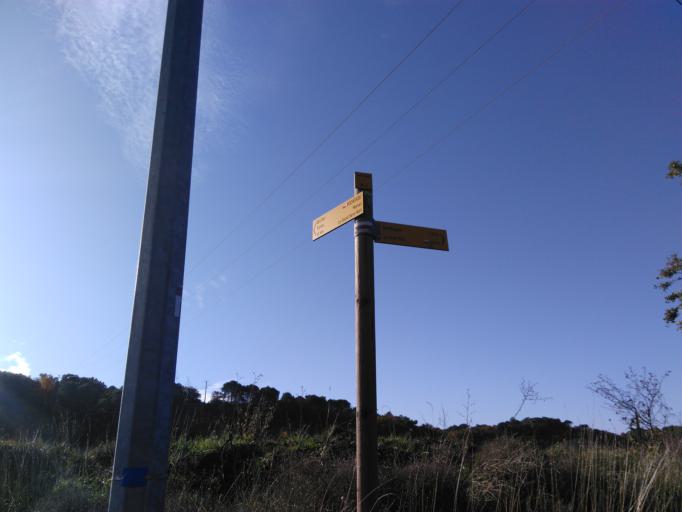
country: FR
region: Provence-Alpes-Cote d'Azur
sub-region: Departement du Vaucluse
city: Mondragon
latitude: 44.2365
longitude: 4.7348
